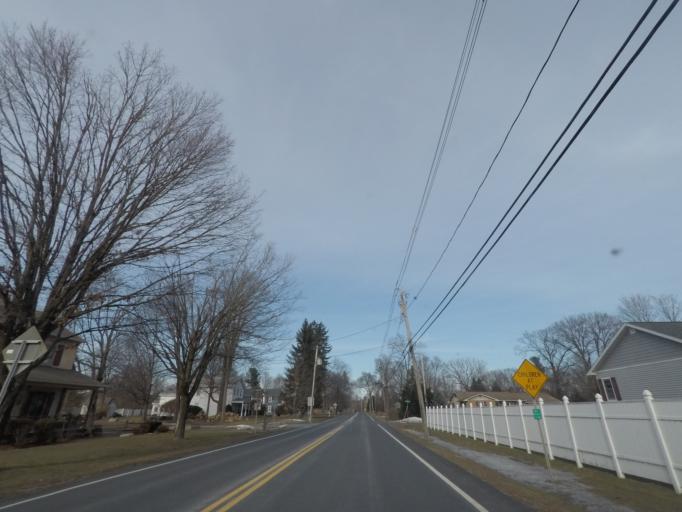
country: US
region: New York
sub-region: Columbia County
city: Valatie
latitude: 42.4075
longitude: -73.6751
